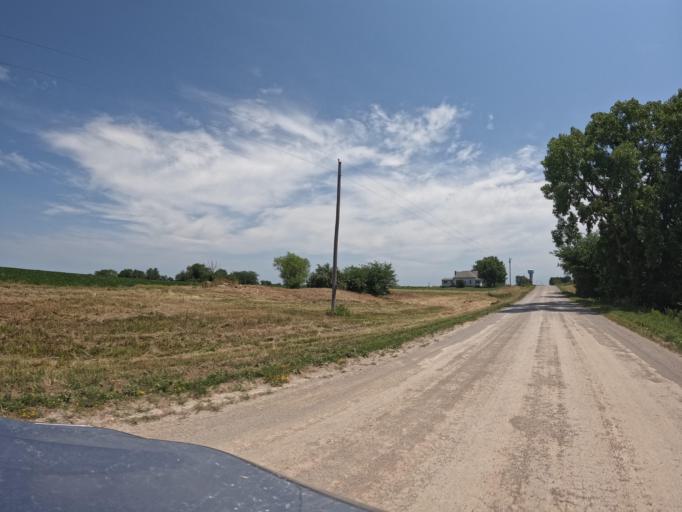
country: US
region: Iowa
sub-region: Appanoose County
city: Centerville
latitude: 40.7868
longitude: -92.9225
